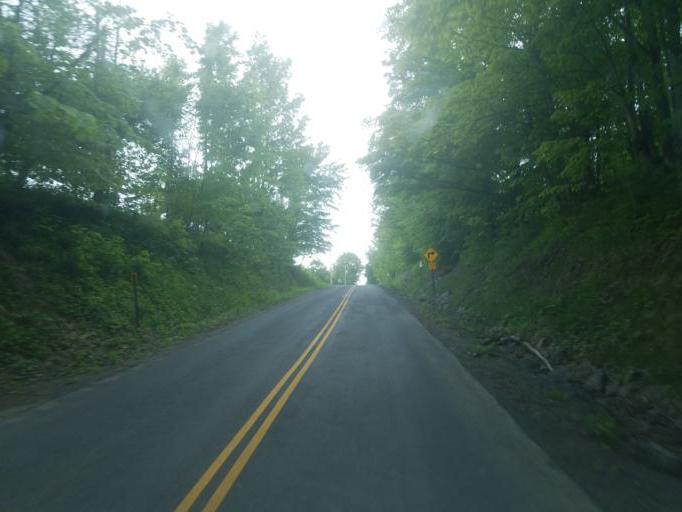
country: US
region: New York
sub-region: Herkimer County
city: Herkimer
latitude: 43.2131
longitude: -74.9531
